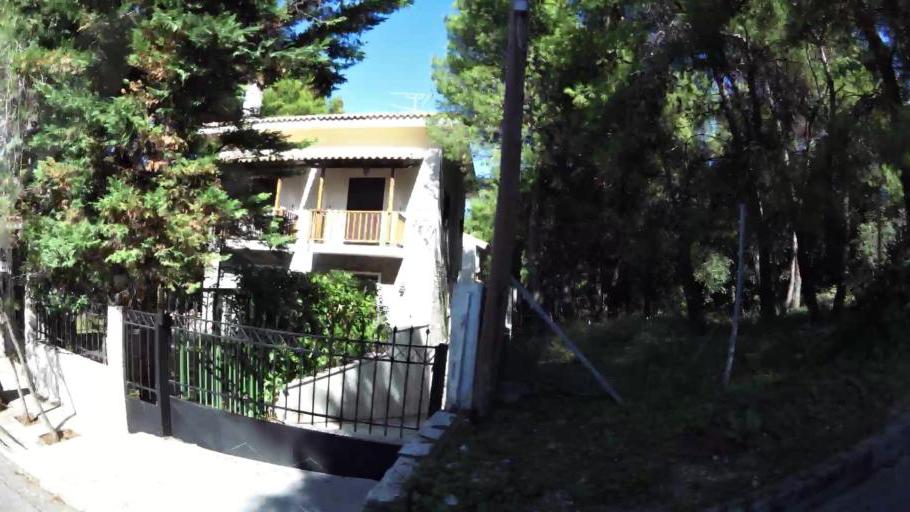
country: GR
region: Attica
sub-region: Nomarchia Anatolikis Attikis
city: Dionysos
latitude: 38.1049
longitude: 23.8864
